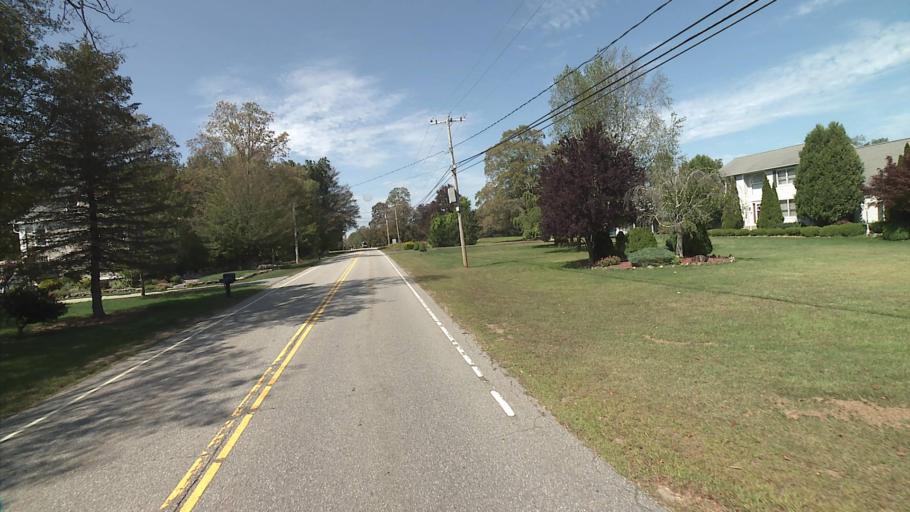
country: US
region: Connecticut
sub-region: Windham County
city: Willimantic
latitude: 41.6796
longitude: -72.2760
